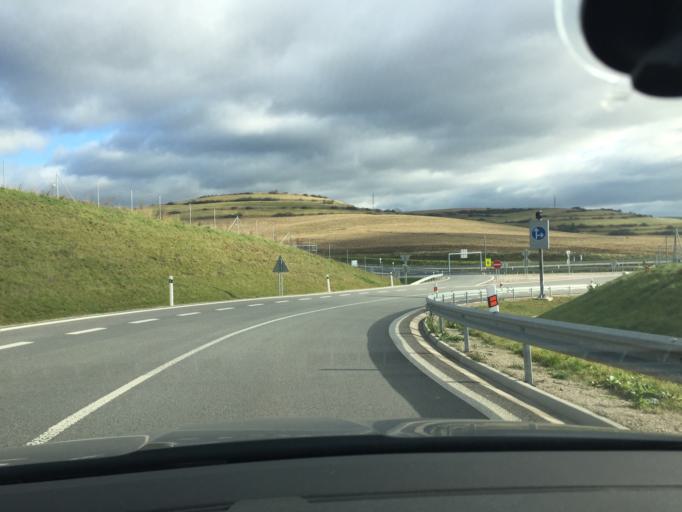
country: SK
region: Presovsky
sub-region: Okres Presov
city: Levoca
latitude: 49.0111
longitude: 20.6027
